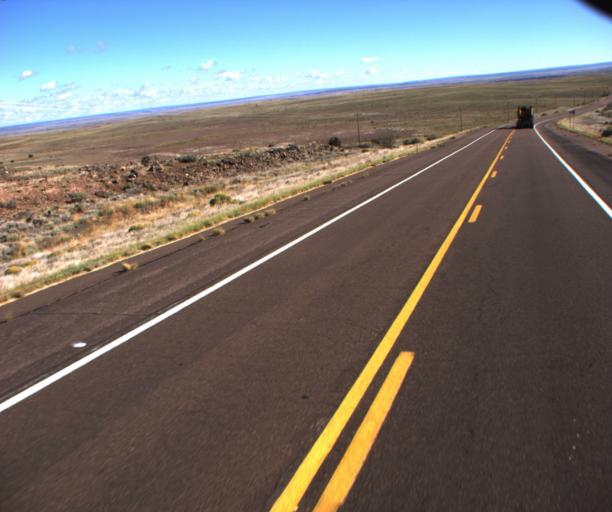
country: US
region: Arizona
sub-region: Apache County
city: Saint Johns
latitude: 34.5006
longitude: -109.4904
